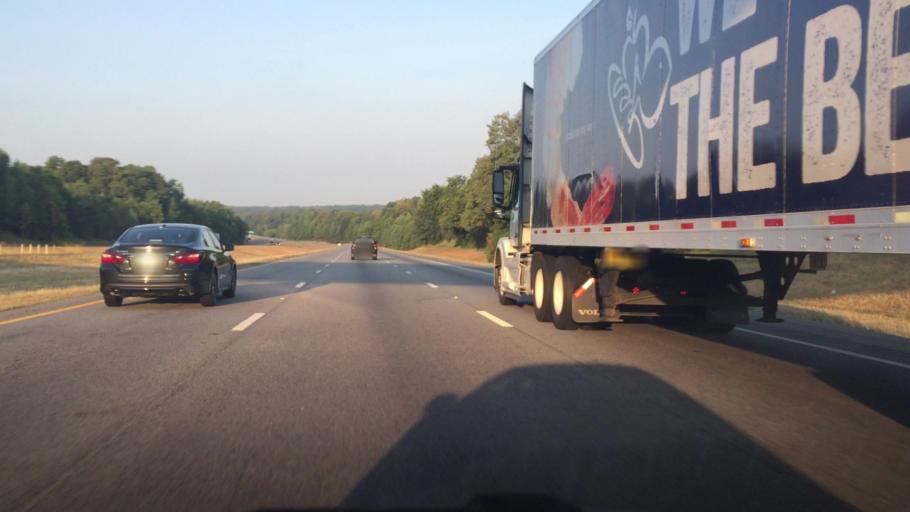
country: US
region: North Carolina
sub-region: Randolph County
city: Trinity
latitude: 35.8876
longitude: -79.9898
